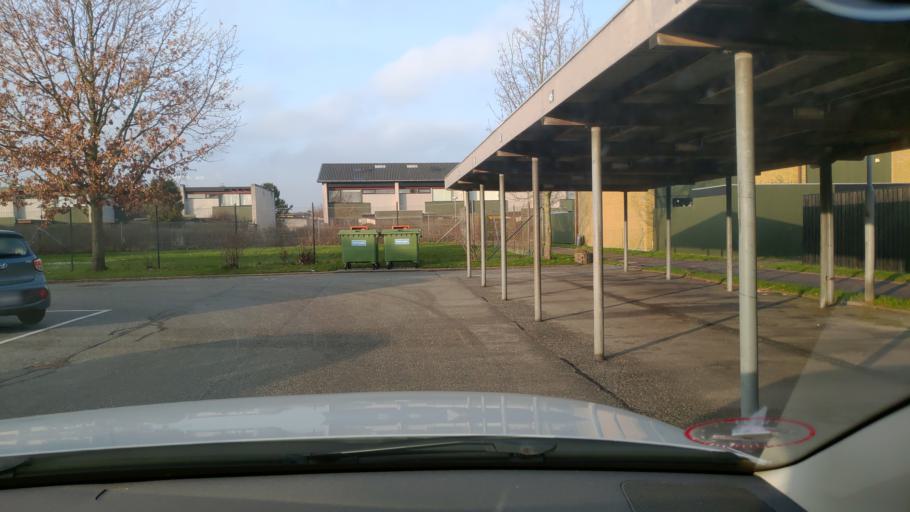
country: DK
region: Zealand
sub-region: Solrod Kommune
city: Solrod Strand
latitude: 55.5418
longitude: 12.2176
